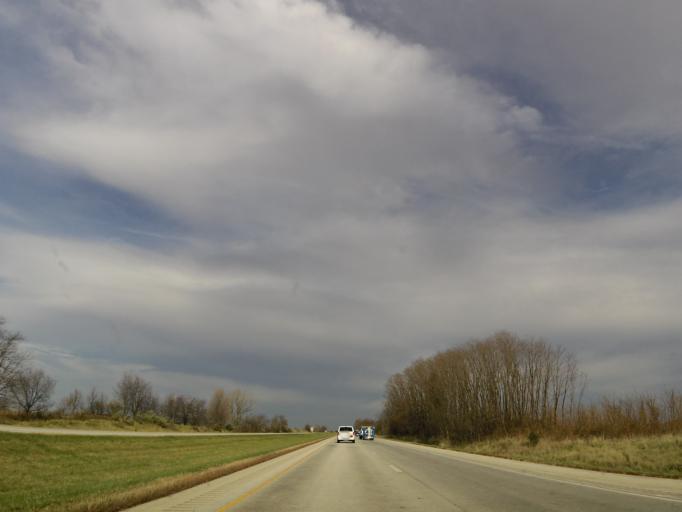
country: US
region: Illinois
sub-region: Knox County
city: Galesburg
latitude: 41.0101
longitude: -90.3348
